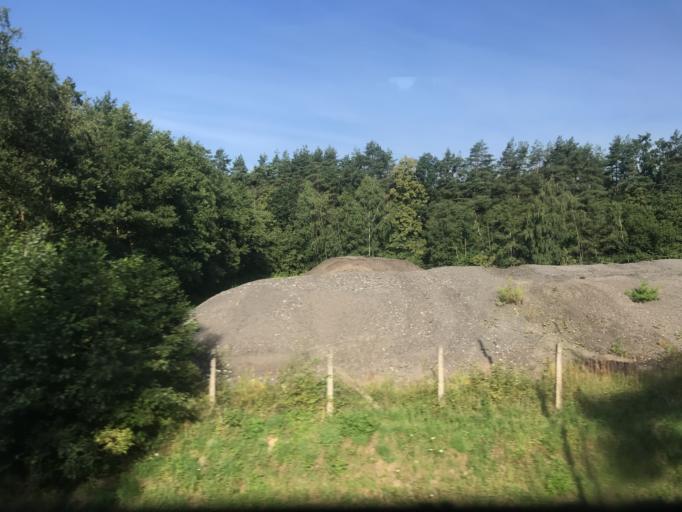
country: CZ
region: Jihocesky
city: Sobeslav
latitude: 49.2332
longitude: 14.7246
